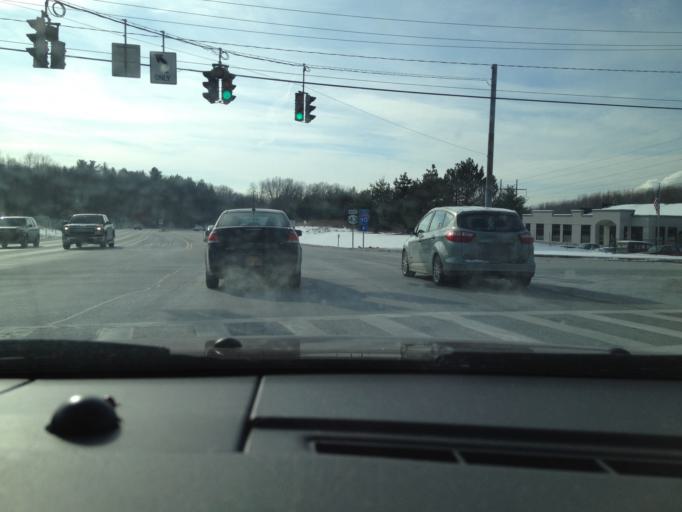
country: US
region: New York
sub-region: Rensselaer County
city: Hampton Manor
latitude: 42.6545
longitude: -73.6993
